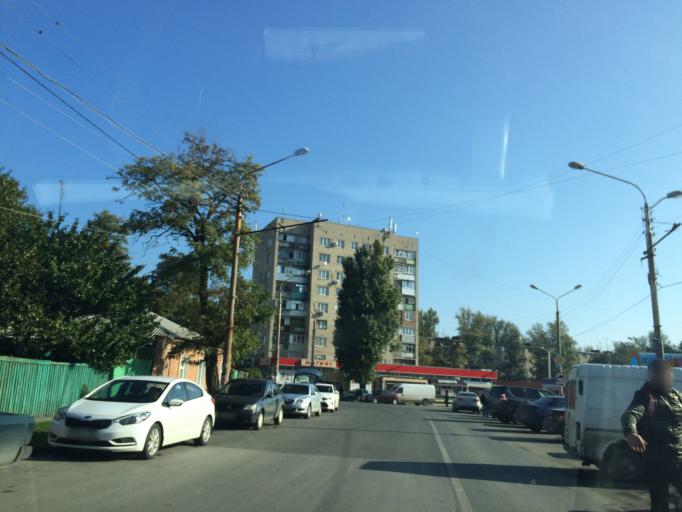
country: RU
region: Rostov
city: Imeni Chkalova
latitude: 47.2671
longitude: 39.7867
